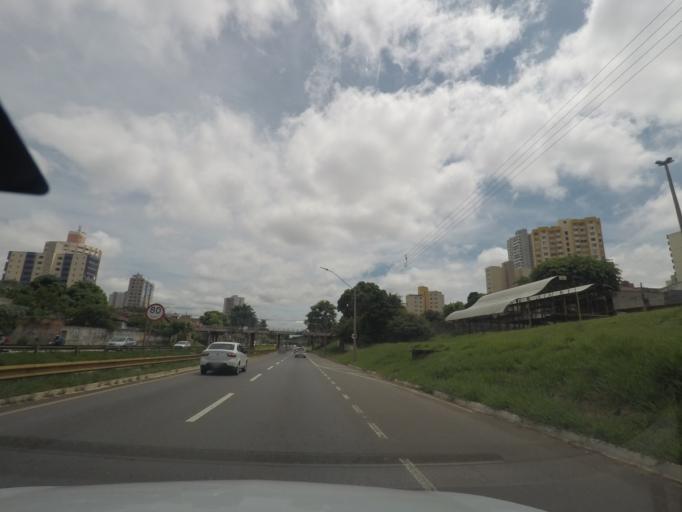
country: BR
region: Goias
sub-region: Goiania
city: Goiania
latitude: -16.6762
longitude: -49.2496
